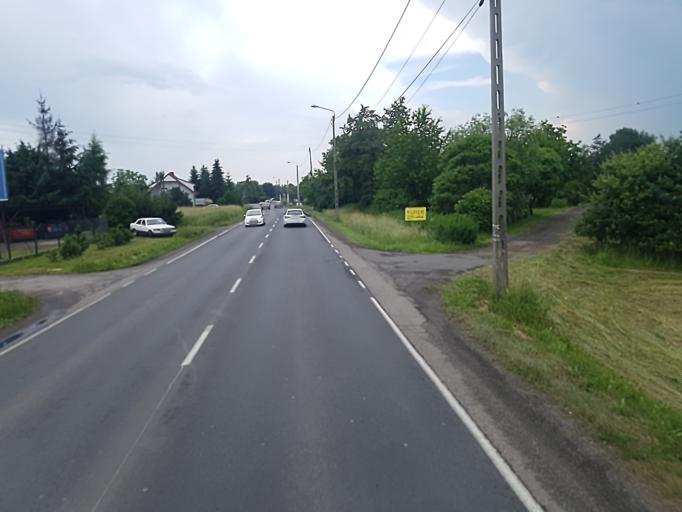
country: PL
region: Silesian Voivodeship
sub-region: Powiat wodzislawski
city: Mszana
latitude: 49.9782
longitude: 18.5201
